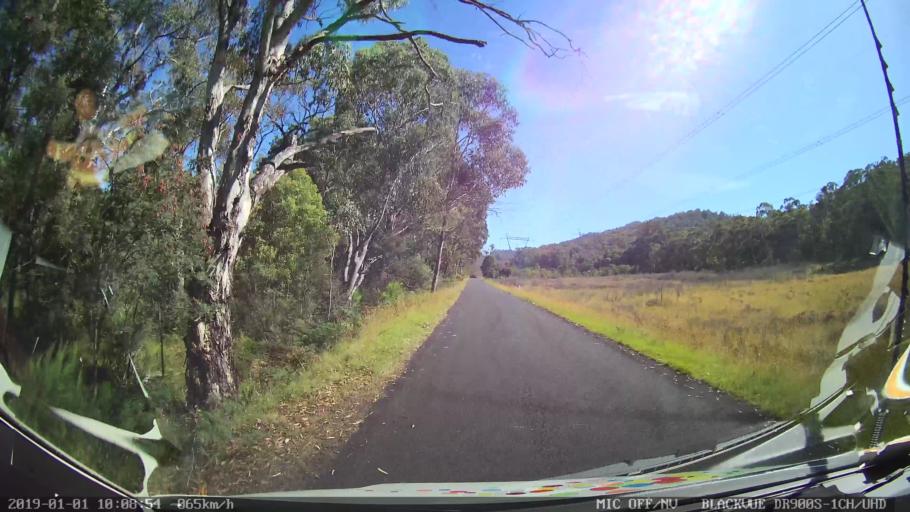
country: AU
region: New South Wales
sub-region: Snowy River
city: Jindabyne
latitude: -36.1548
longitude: 148.1579
